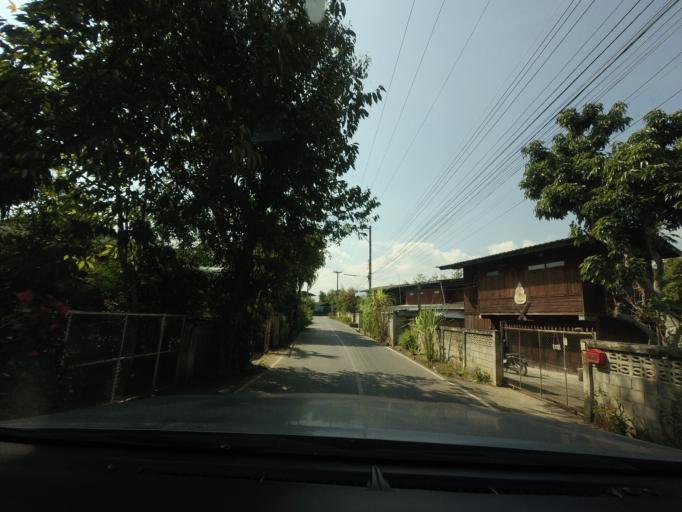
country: TH
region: Mae Hong Son
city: Wiang Nuea
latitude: 19.3931
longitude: 98.4432
